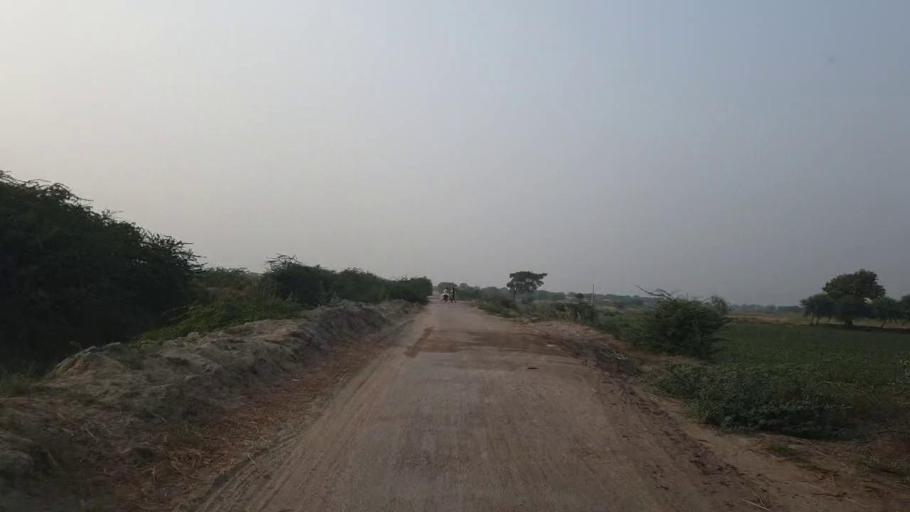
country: PK
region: Sindh
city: Mirpur Batoro
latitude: 24.6474
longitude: 68.3918
